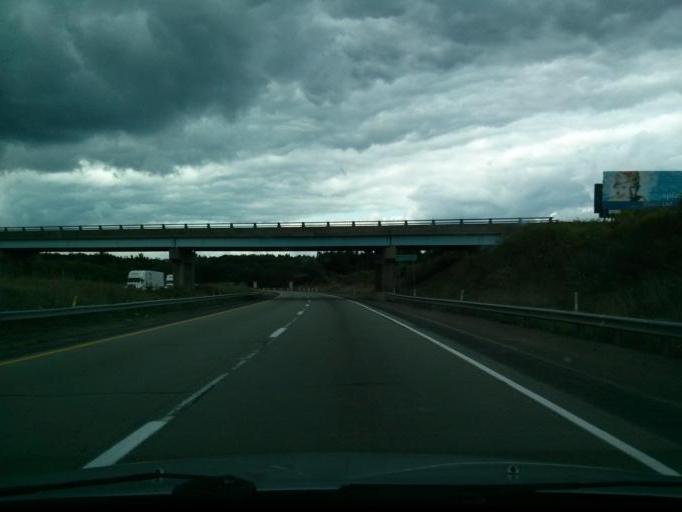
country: US
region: Pennsylvania
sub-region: Clarion County
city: Clarion
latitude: 41.1877
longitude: -79.2356
